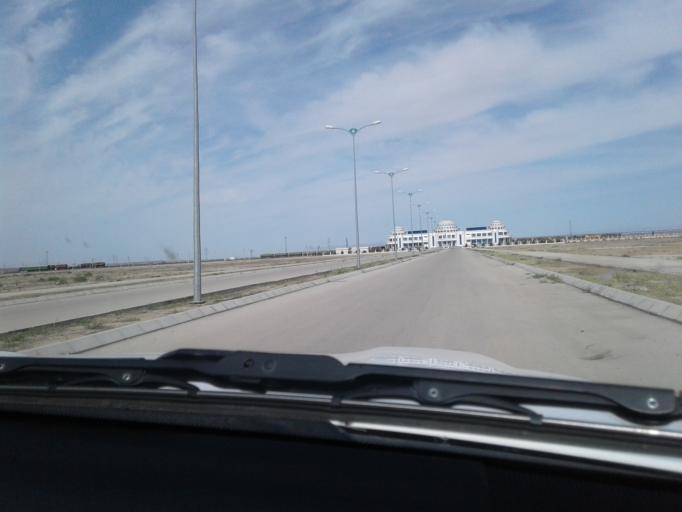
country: TM
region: Balkan
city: Gazanjyk
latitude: 39.2663
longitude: 55.4952
